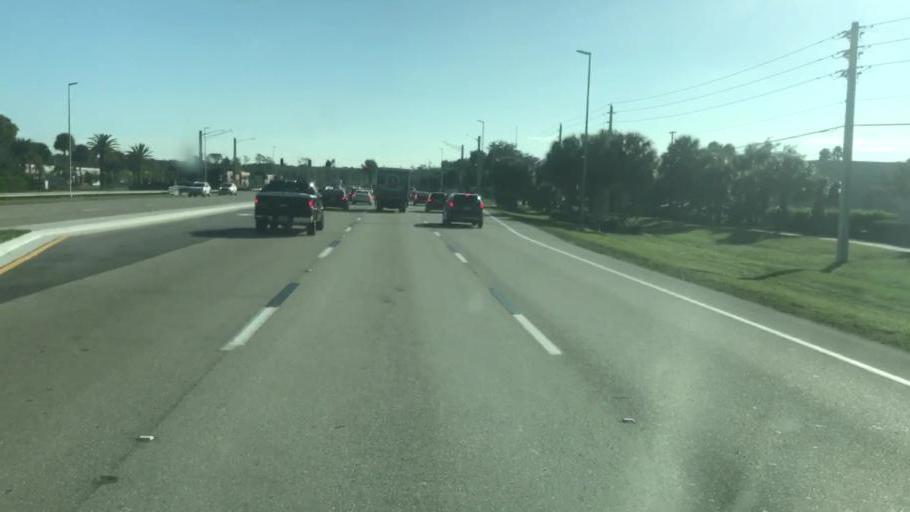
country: US
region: Florida
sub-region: Lee County
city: Villas
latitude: 26.5465
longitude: -81.8450
